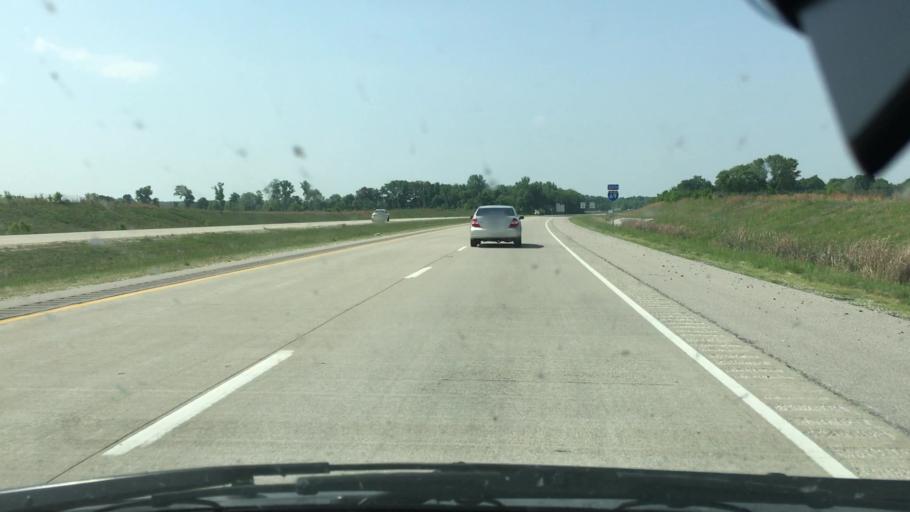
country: US
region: Indiana
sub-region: Daviess County
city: Washington
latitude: 38.6472
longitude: -87.1212
